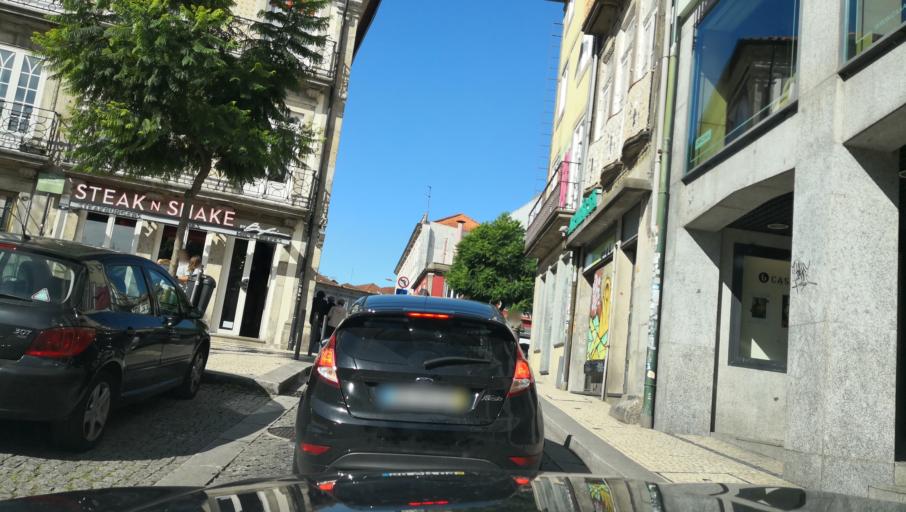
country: PT
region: Porto
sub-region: Porto
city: Porto
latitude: 41.1479
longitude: -8.6147
